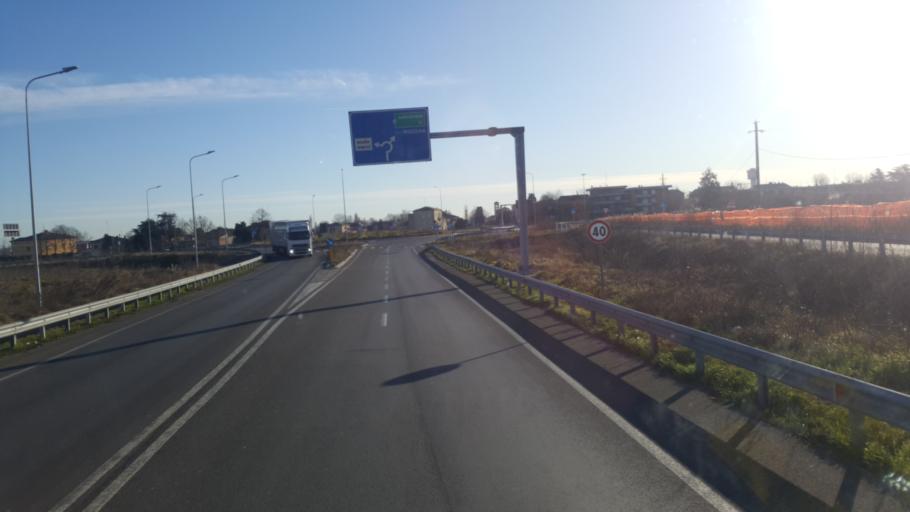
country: IT
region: Emilia-Romagna
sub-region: Provincia di Modena
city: Campogalliano
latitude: 44.6485
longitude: 10.8362
